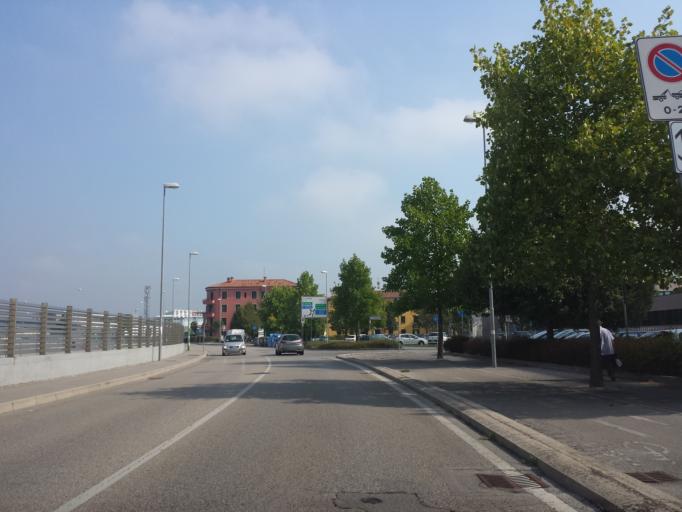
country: IT
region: Veneto
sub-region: Provincia di Padova
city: Padova
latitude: 45.4149
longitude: 11.8935
